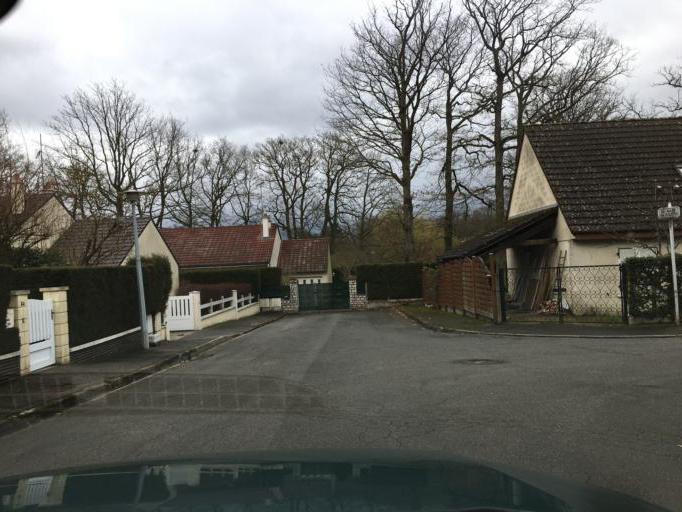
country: FR
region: Centre
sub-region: Departement du Loiret
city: Saran
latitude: 47.9559
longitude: 1.8807
